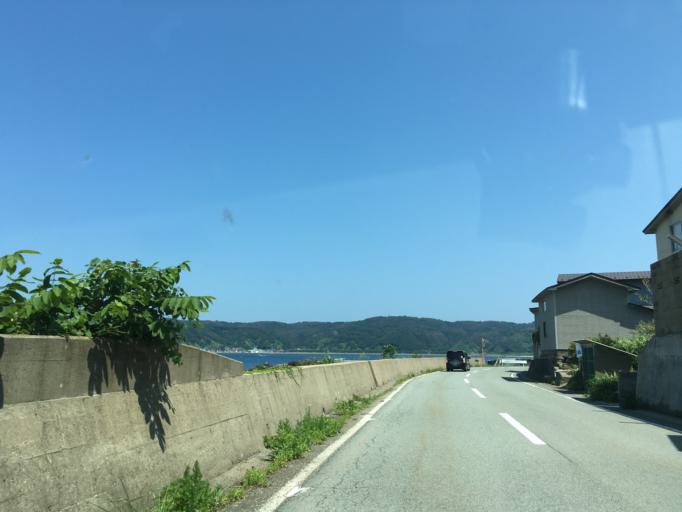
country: JP
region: Akita
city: Tenno
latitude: 39.9459
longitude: 139.7091
